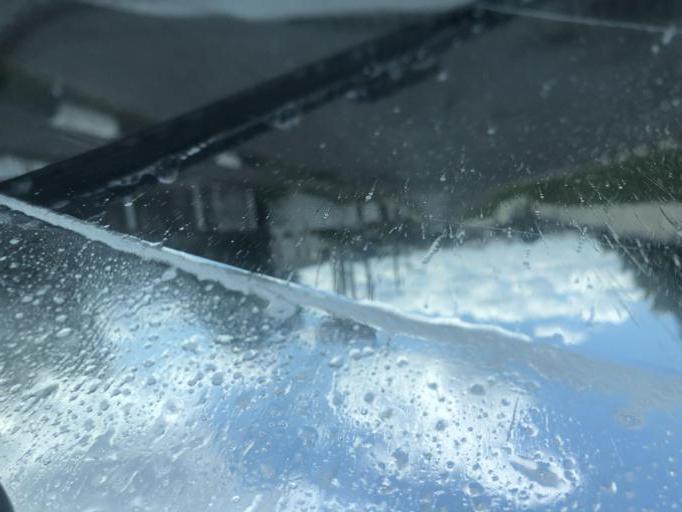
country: BR
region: Santa Catarina
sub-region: Lages
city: Lages
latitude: -27.7907
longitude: -50.3116
